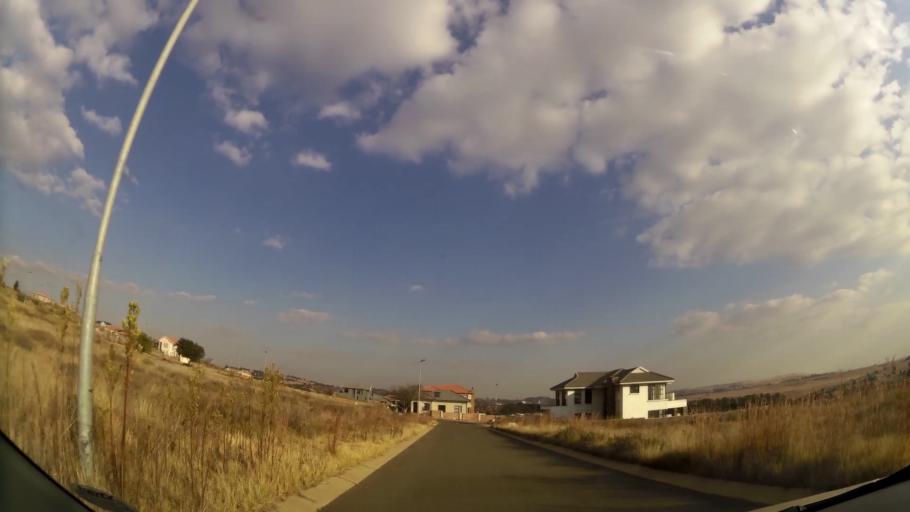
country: ZA
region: Gauteng
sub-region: West Rand District Municipality
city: Krugersdorp
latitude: -26.1008
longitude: 27.7294
